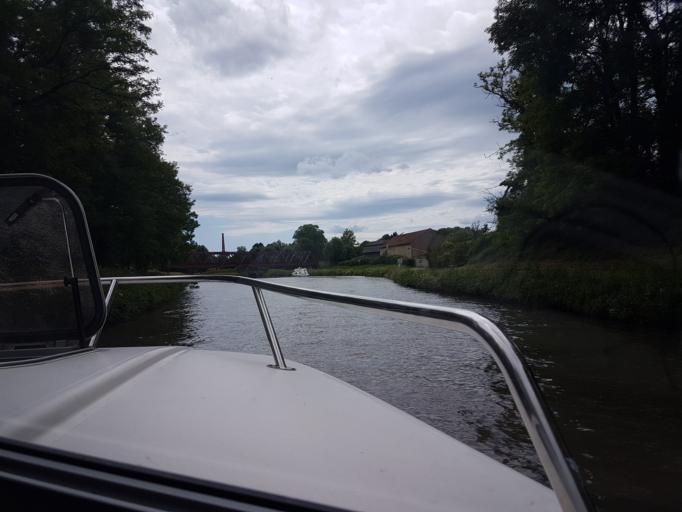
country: FR
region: Bourgogne
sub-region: Departement de la Nievre
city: Clamecy
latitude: 47.4797
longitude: 3.5242
